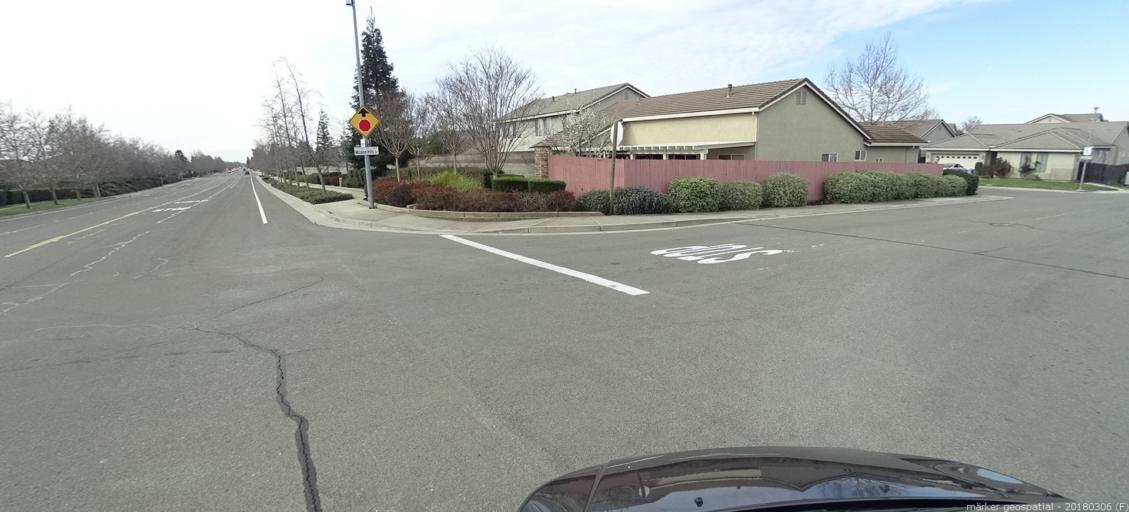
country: US
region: California
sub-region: Sacramento County
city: Vineyard
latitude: 38.4741
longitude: -121.3162
